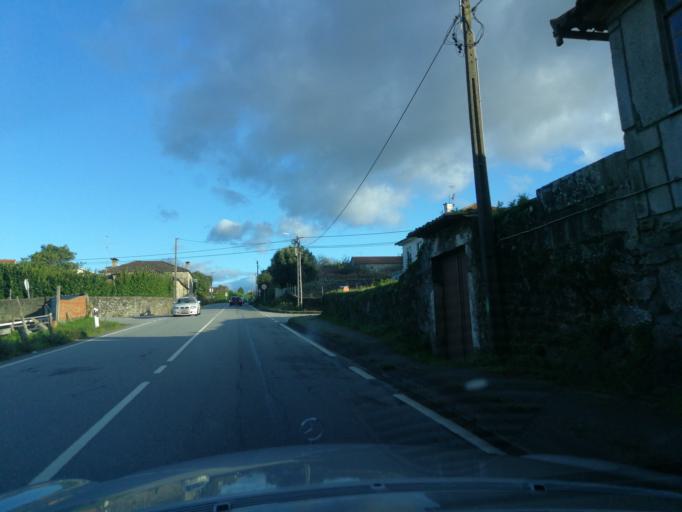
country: PT
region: Braga
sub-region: Esposende
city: Marinhas
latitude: 41.6159
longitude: -8.7500
